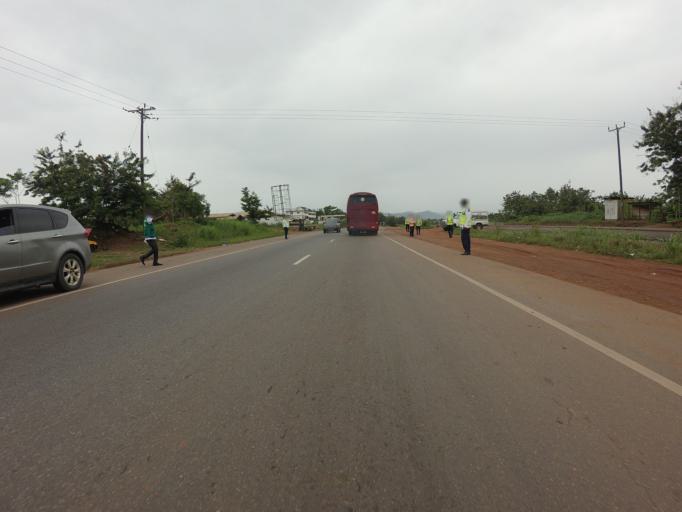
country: GH
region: Eastern
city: Suhum
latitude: 6.0533
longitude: -0.4635
